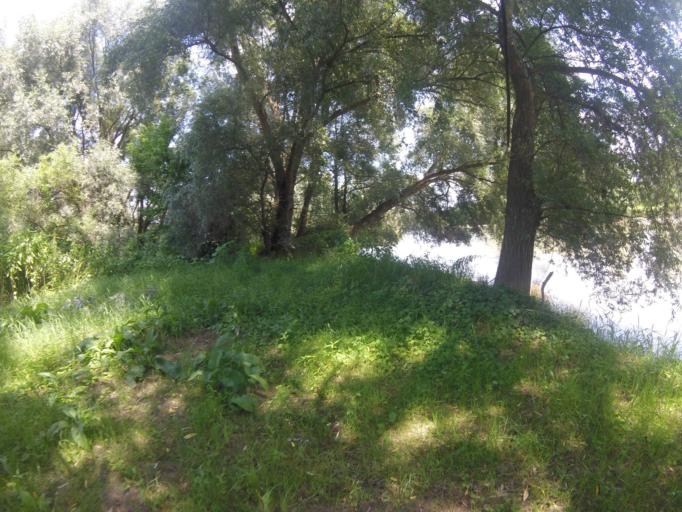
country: HU
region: Zala
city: Murakeresztur
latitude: 46.3545
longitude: 16.8610
